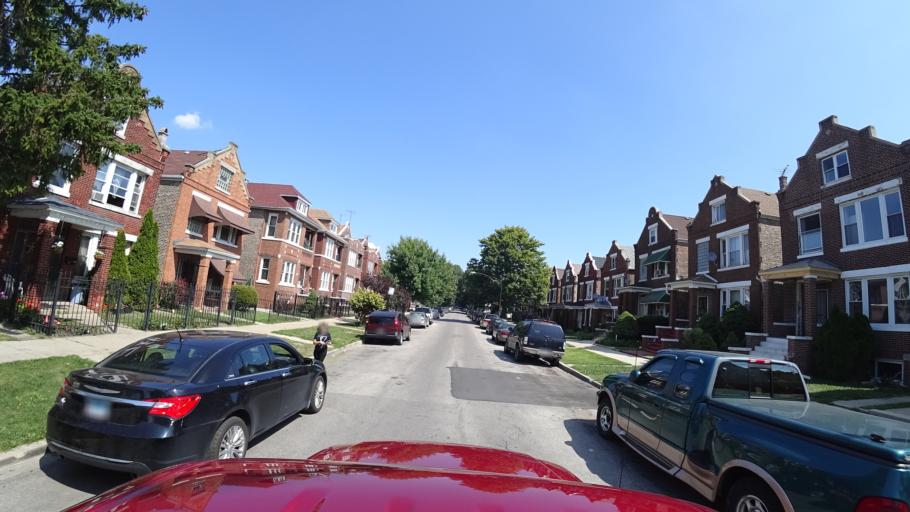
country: US
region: Illinois
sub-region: Cook County
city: Chicago
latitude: 41.8125
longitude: -87.6871
